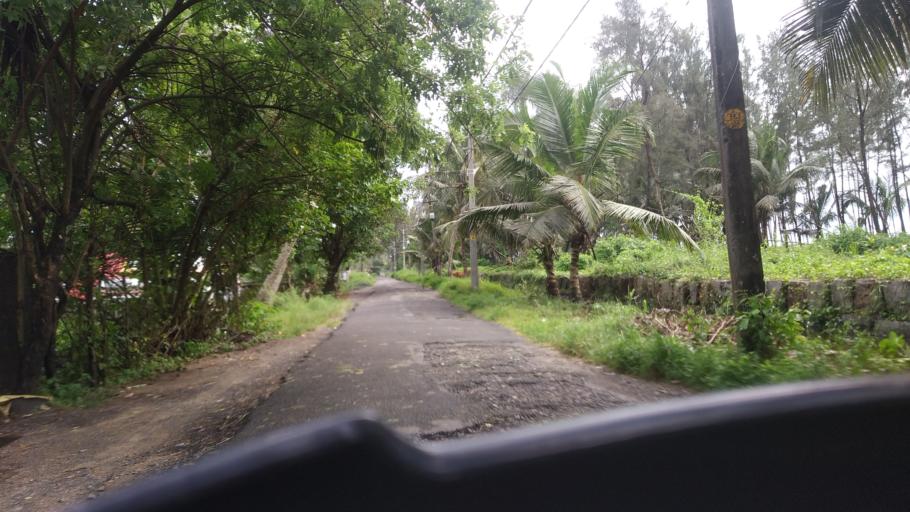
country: IN
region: Kerala
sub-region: Ernakulam
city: Elur
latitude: 10.1135
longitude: 76.1869
